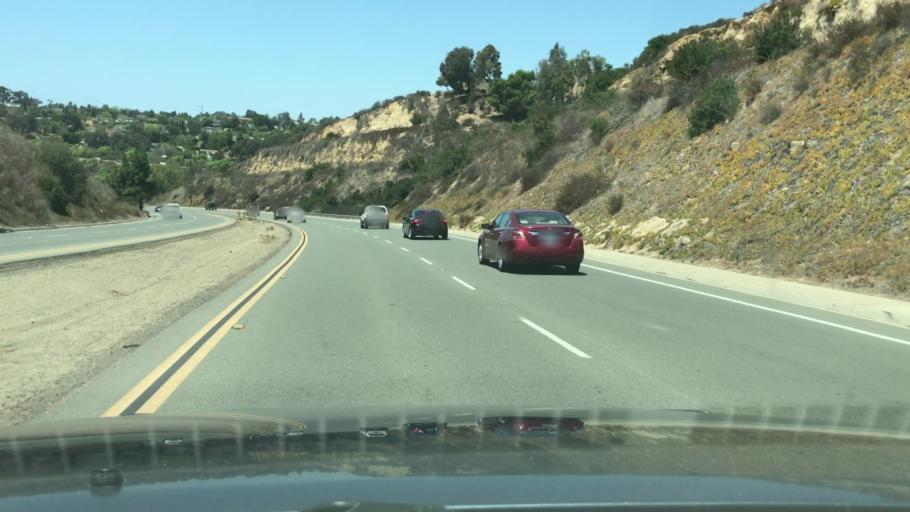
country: US
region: California
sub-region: San Diego County
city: La Jolla
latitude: 32.8415
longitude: -117.1972
